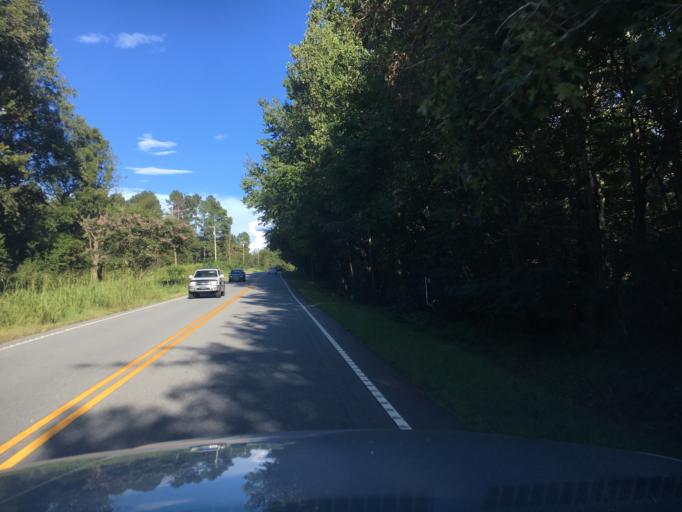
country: US
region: South Carolina
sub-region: Greenville County
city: Five Forks
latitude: 34.7924
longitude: -82.1320
